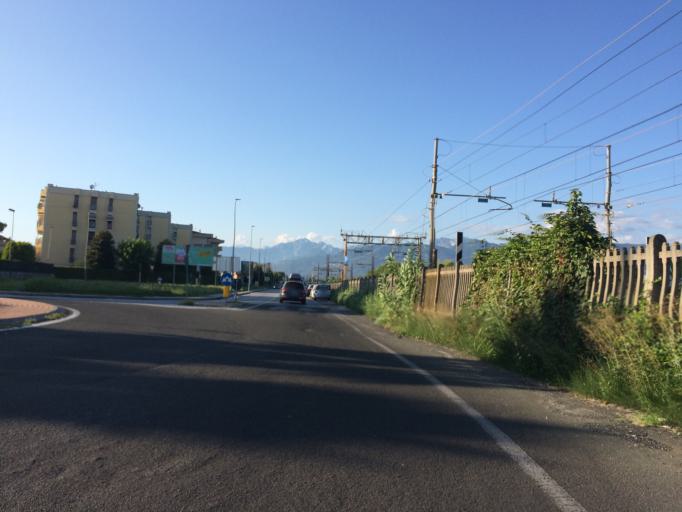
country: IT
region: Tuscany
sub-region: Provincia di Lucca
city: Viareggio
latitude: 43.8818
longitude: 10.2510
